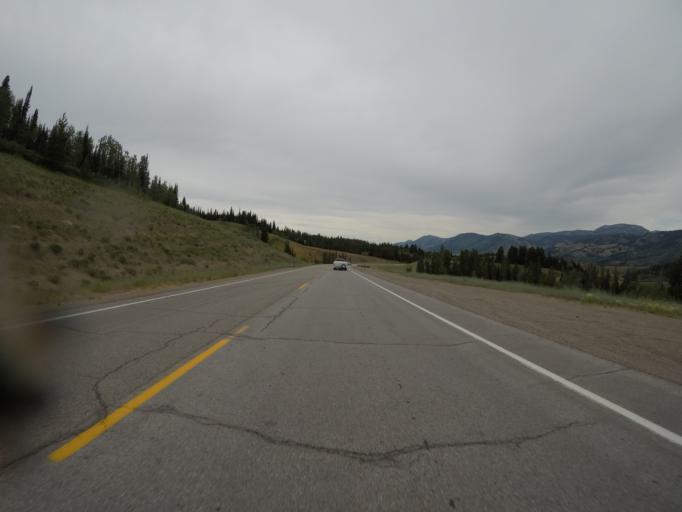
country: US
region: Wyoming
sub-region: Lincoln County
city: Afton
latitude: 42.5110
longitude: -110.9095
